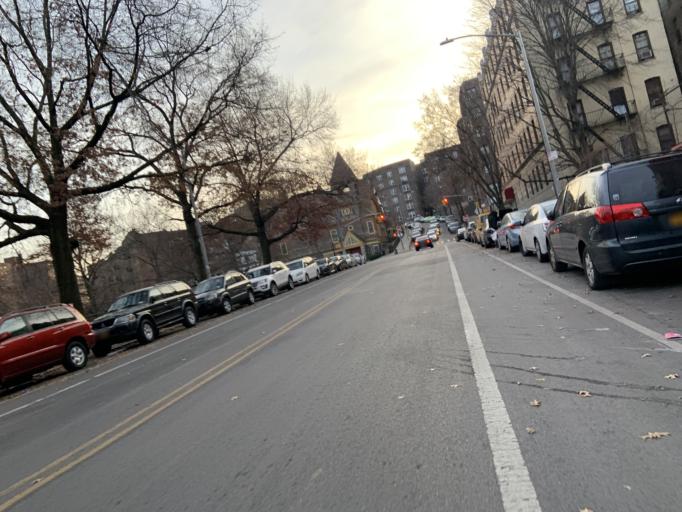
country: US
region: New York
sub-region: New York County
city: Inwood
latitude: 40.8778
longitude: -73.9085
